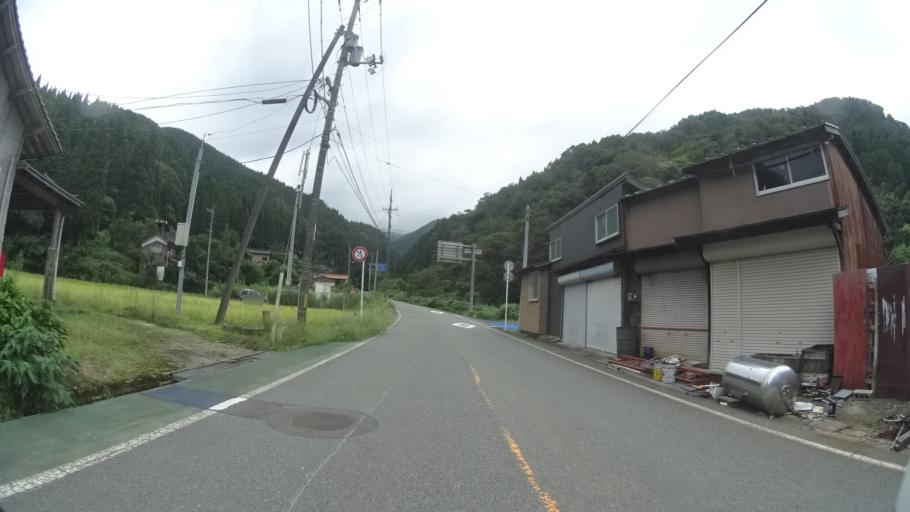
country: JP
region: Tottori
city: Kurayoshi
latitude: 35.4148
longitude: 134.0193
